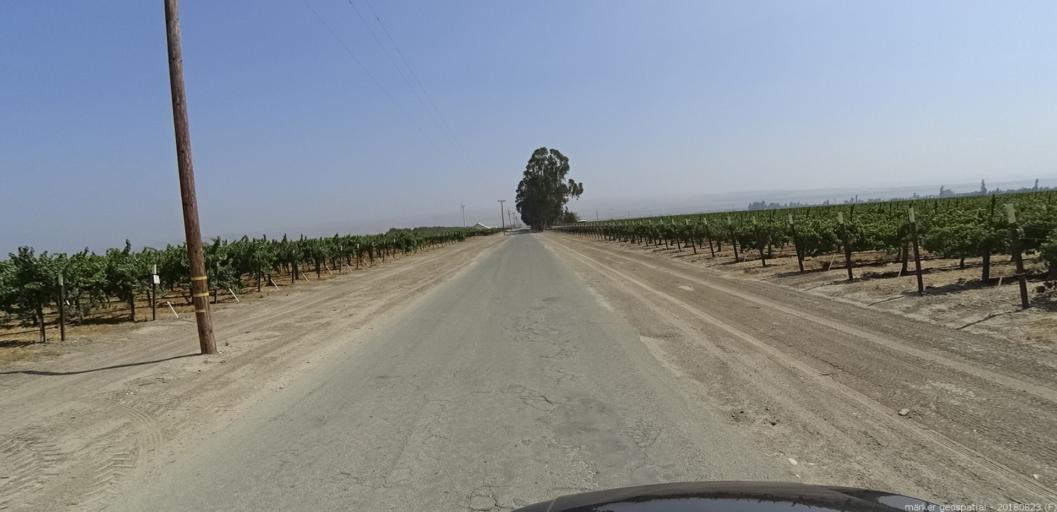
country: US
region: California
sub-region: Monterey County
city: Greenfield
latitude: 36.2654
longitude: -121.2046
